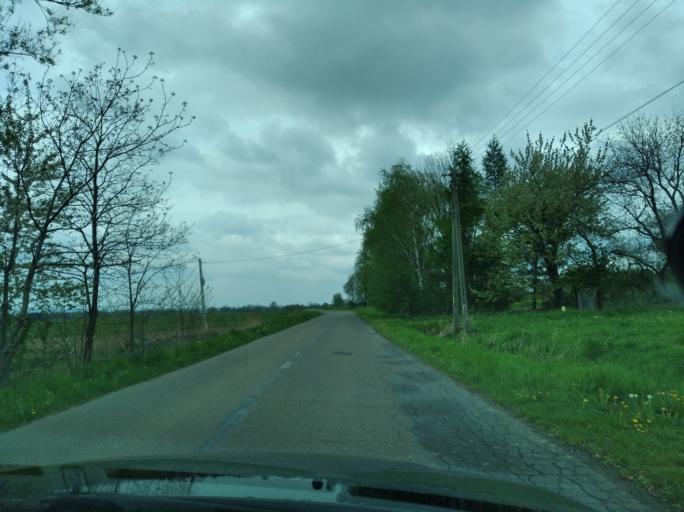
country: PL
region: Subcarpathian Voivodeship
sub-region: Powiat brzozowski
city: Gorki
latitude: 49.6125
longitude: 22.0418
